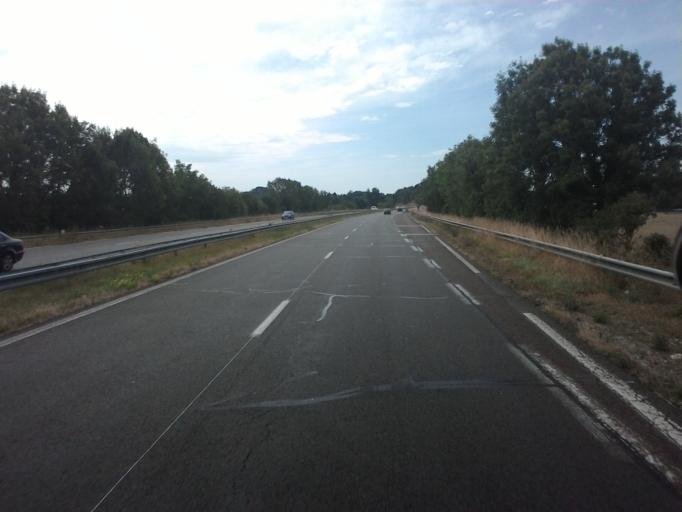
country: FR
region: Franche-Comte
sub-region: Departement du Jura
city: Montmorot
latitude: 46.7623
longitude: 5.5560
